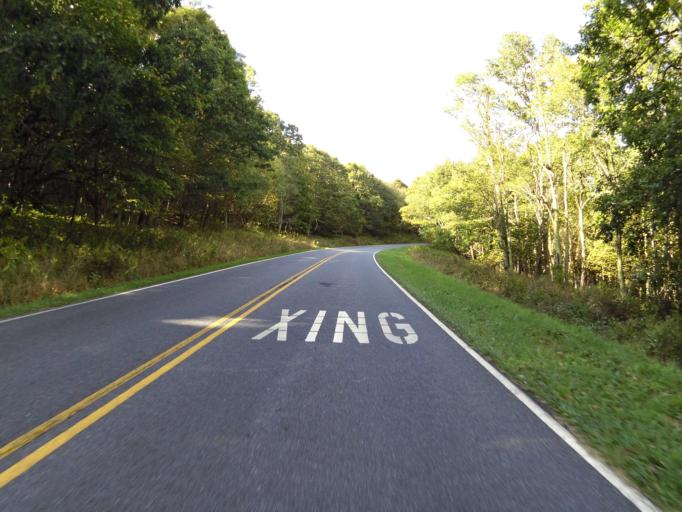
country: US
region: Virginia
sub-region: Page County
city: Luray
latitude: 38.5820
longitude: -78.3837
